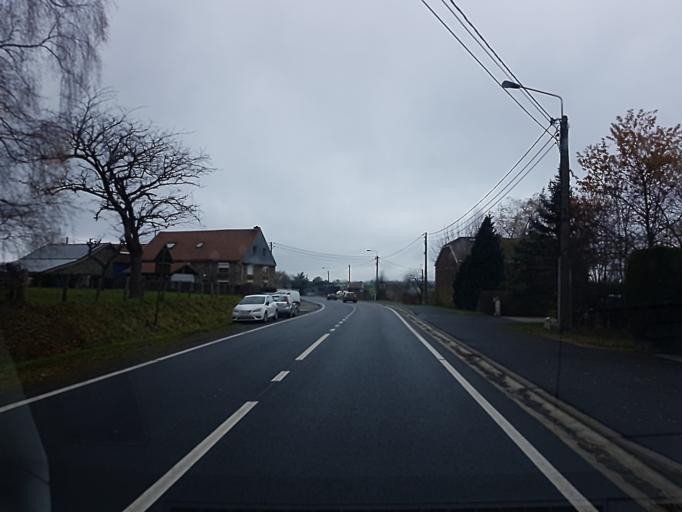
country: BE
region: Wallonia
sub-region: Province de Liege
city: Jalhay
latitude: 50.5592
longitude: 5.9547
